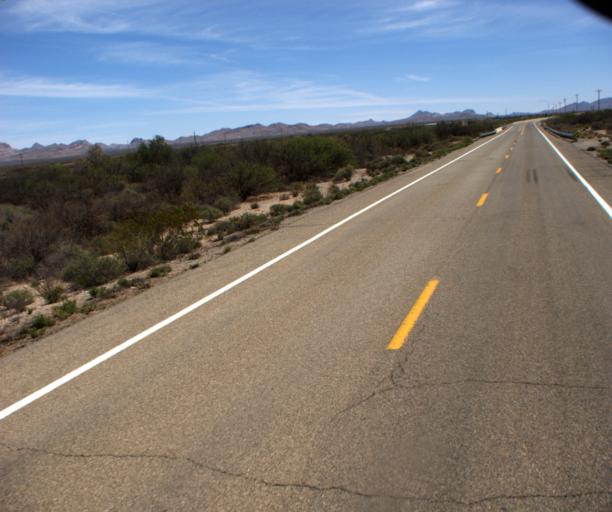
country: US
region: New Mexico
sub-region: Hidalgo County
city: Lordsburg
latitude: 32.2605
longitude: -109.2011
